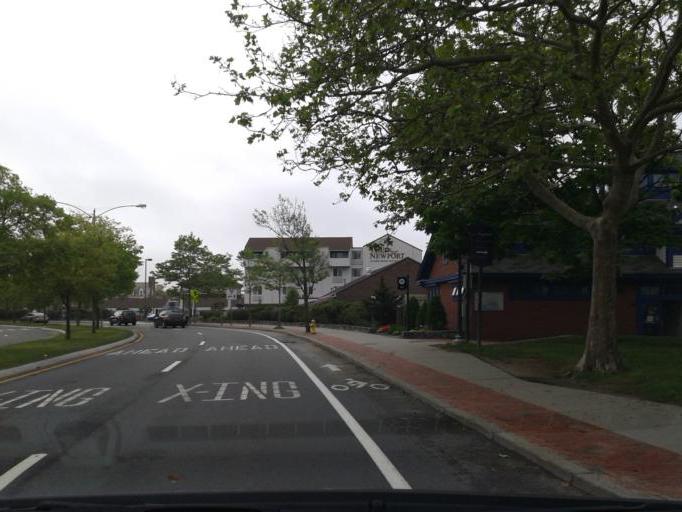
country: US
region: Rhode Island
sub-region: Newport County
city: Newport
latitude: 41.4888
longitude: -71.3169
